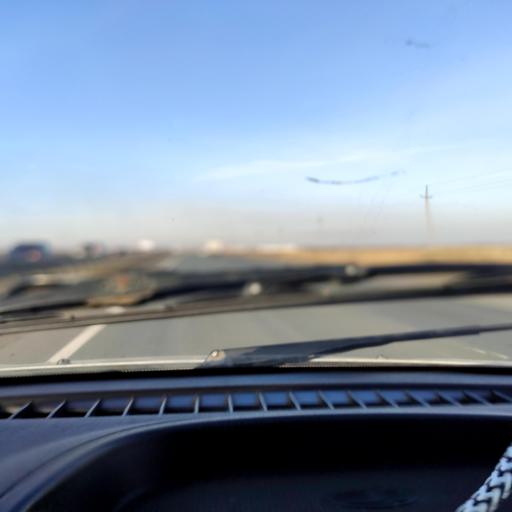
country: RU
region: Samara
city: Zhigulevsk
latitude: 53.5461
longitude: 49.5111
